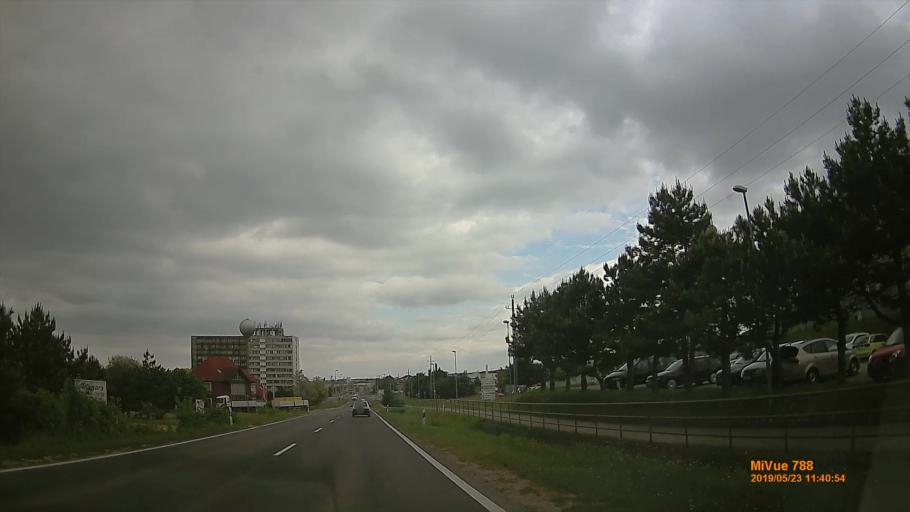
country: HU
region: Veszprem
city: Veszprem
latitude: 47.1133
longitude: 17.8791
